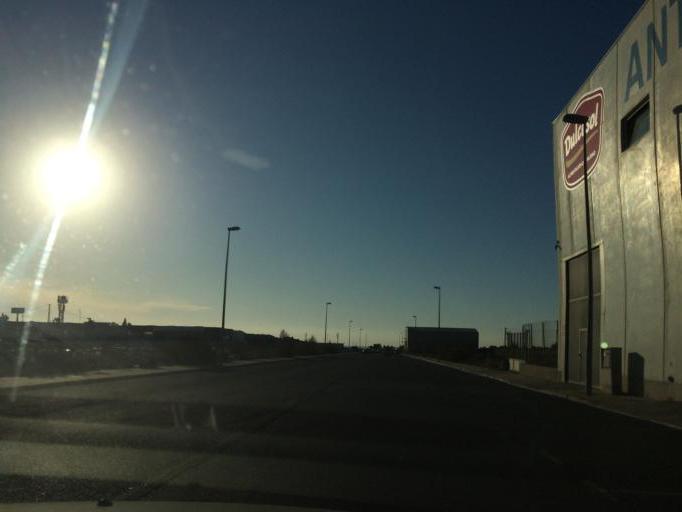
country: ES
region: Andalusia
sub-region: Provincia de Almeria
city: Viator
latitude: 36.8784
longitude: -2.4119
